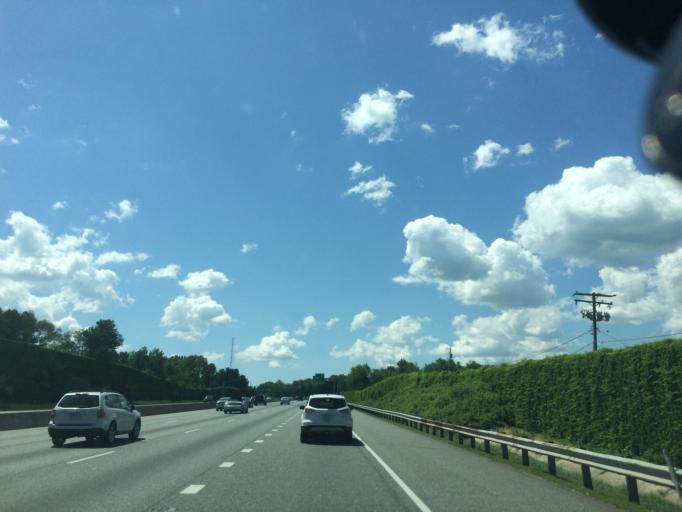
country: US
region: Maryland
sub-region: Baltimore County
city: Catonsville
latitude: 39.2966
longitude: -76.7430
